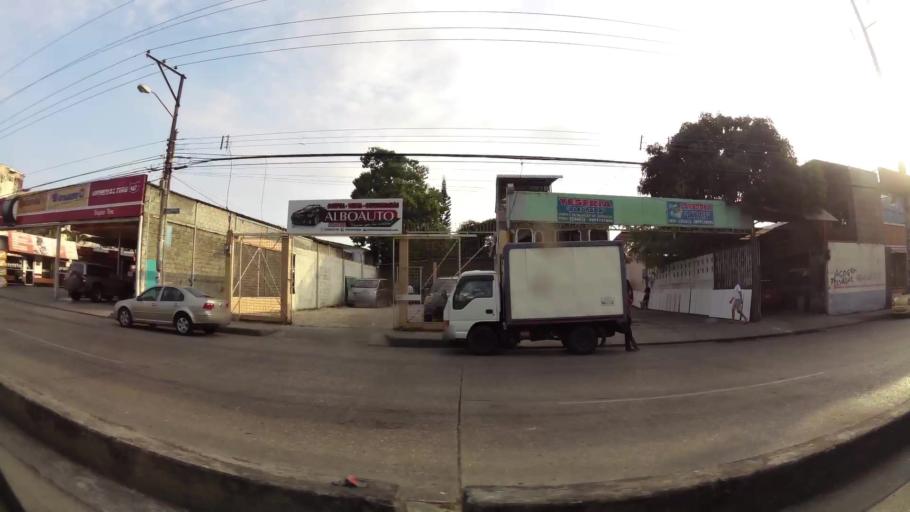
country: EC
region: Guayas
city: Eloy Alfaro
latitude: -2.1351
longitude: -79.8947
